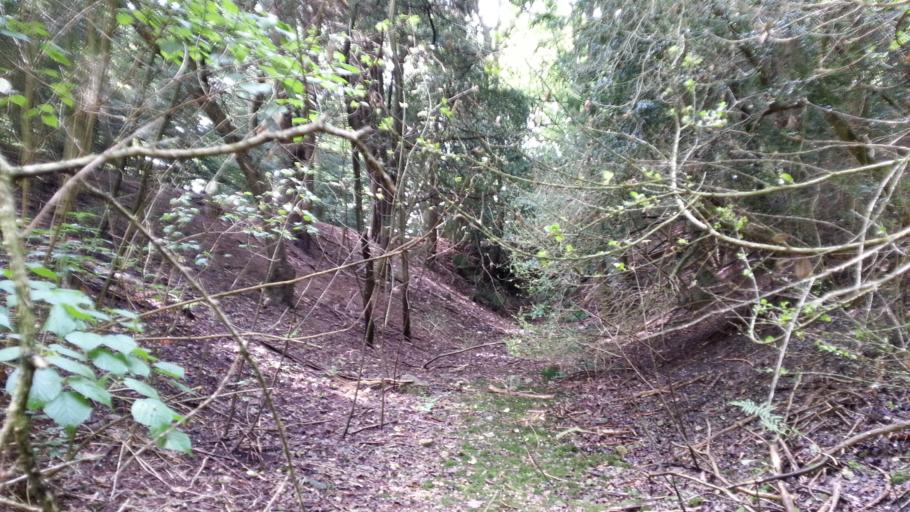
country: FR
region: Picardie
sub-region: Departement de l'Oise
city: Saint-Maximin
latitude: 49.2351
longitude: 2.4502
